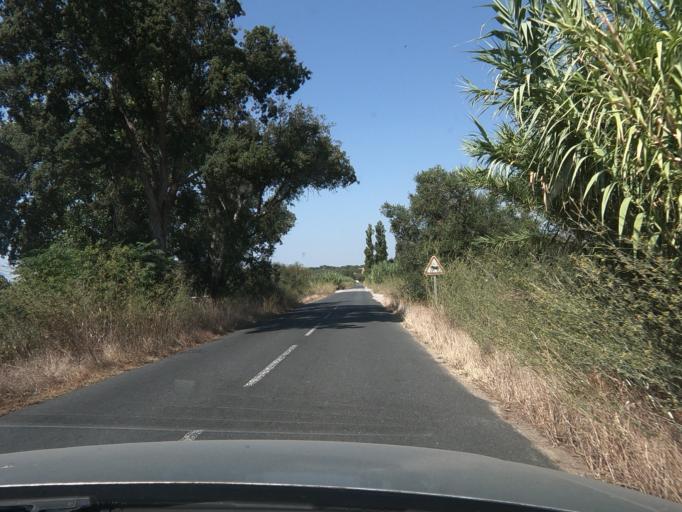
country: PT
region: Setubal
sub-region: Alcacer do Sal
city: Alcacer do Sal
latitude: 38.2843
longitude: -8.4010
